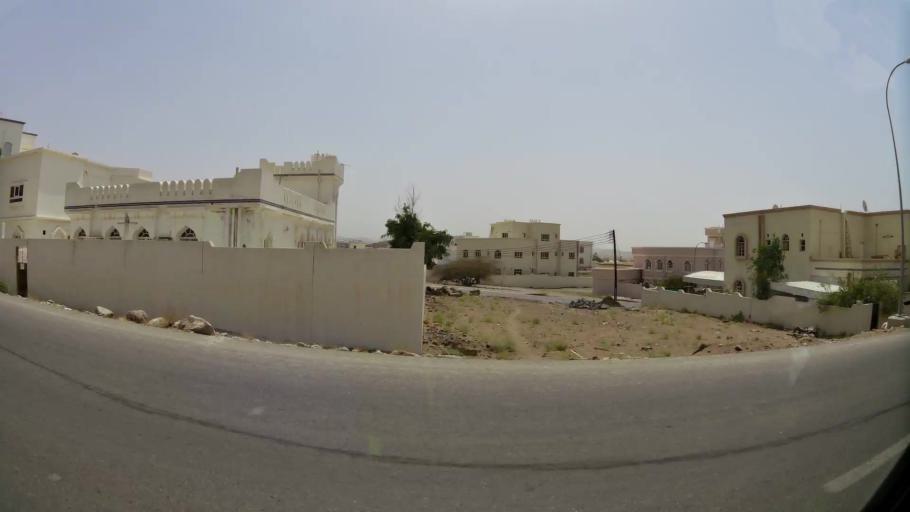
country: OM
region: Muhafazat Masqat
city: Bawshar
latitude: 23.5350
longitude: 58.3857
